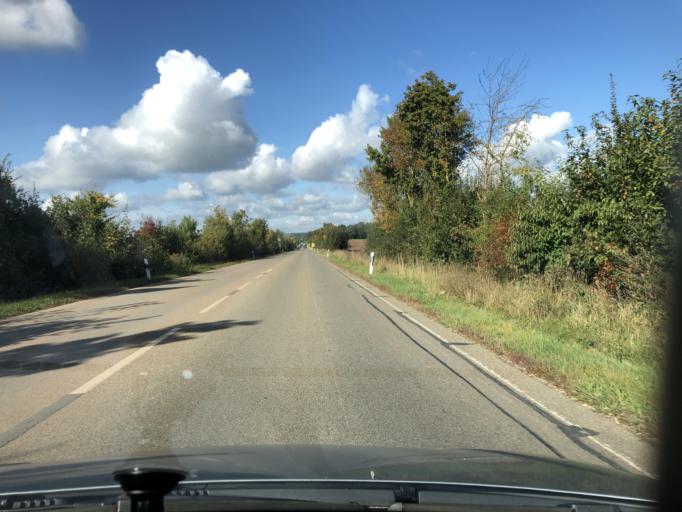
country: DE
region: Bavaria
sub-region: Regierungsbezirk Mittelfranken
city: Puschendorf
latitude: 49.4919
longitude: 10.8387
